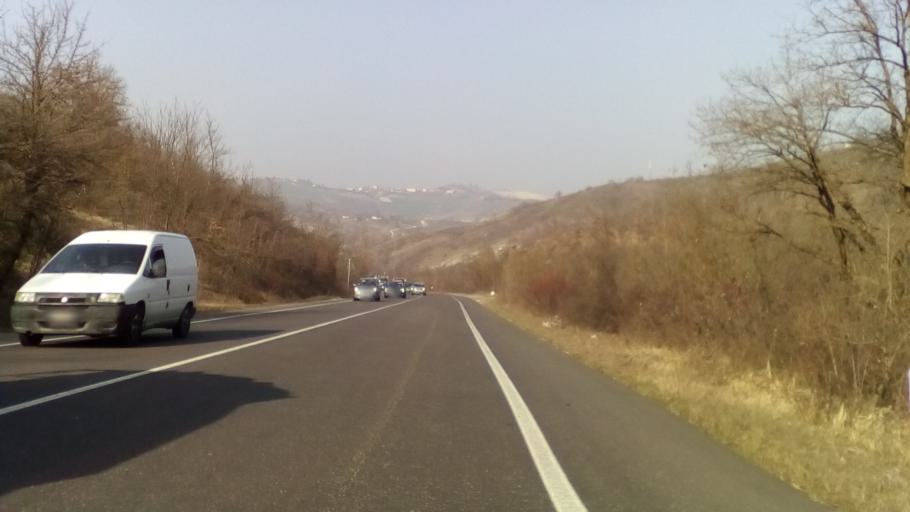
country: IT
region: Emilia-Romagna
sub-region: Provincia di Modena
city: Serramazzoni
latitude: 44.4506
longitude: 10.8351
